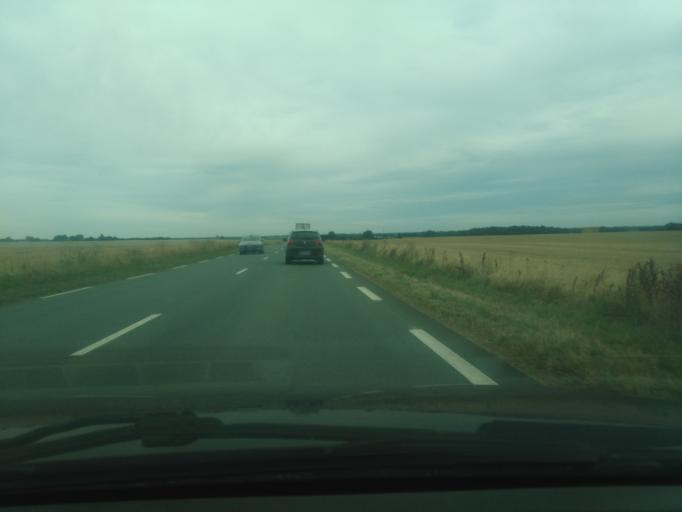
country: FR
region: Poitou-Charentes
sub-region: Departement de la Vienne
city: Saint-Savin
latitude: 46.5714
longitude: 0.8208
